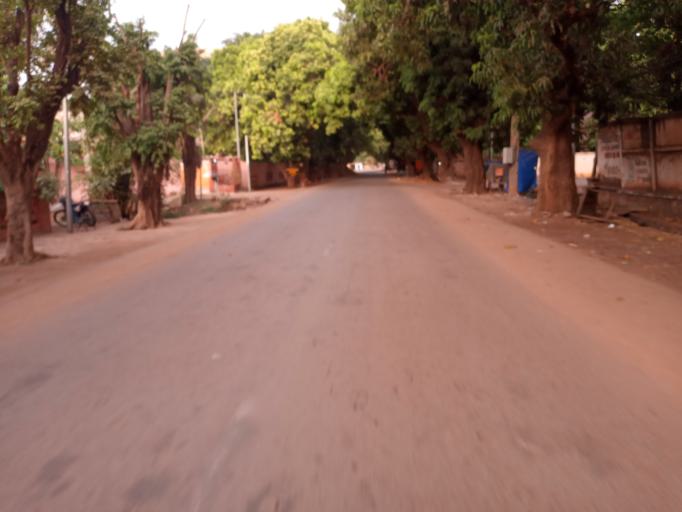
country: ML
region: Bamako
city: Bamako
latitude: 12.6349
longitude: -7.9983
